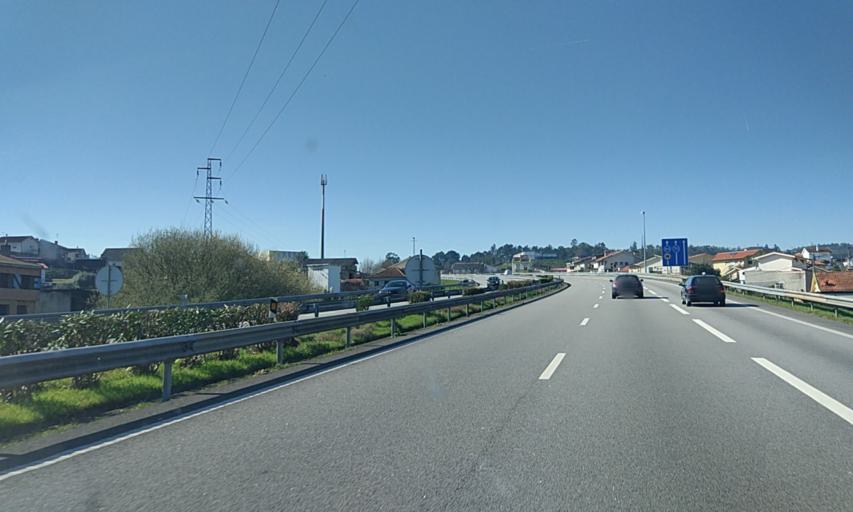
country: PT
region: Porto
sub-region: Valongo
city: Campo
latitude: 41.1857
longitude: -8.4629
